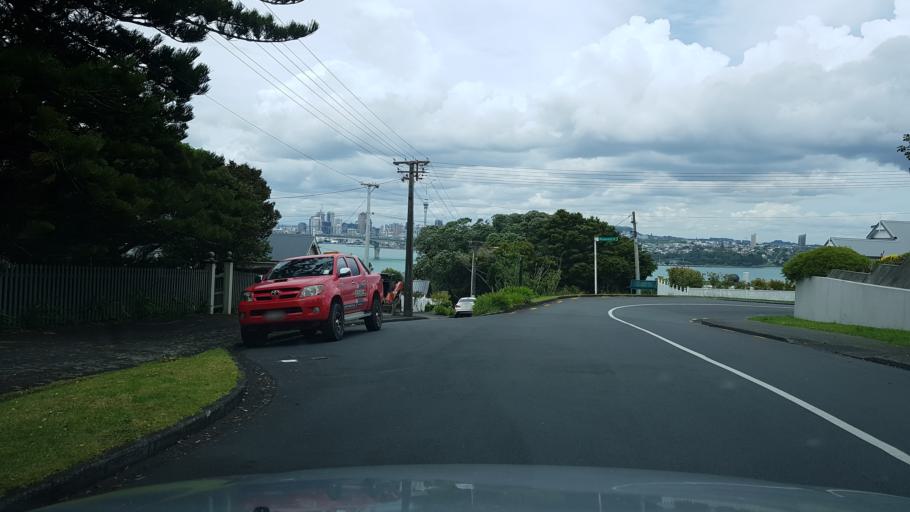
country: NZ
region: Auckland
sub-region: Auckland
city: North Shore
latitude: -36.8197
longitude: 174.7342
